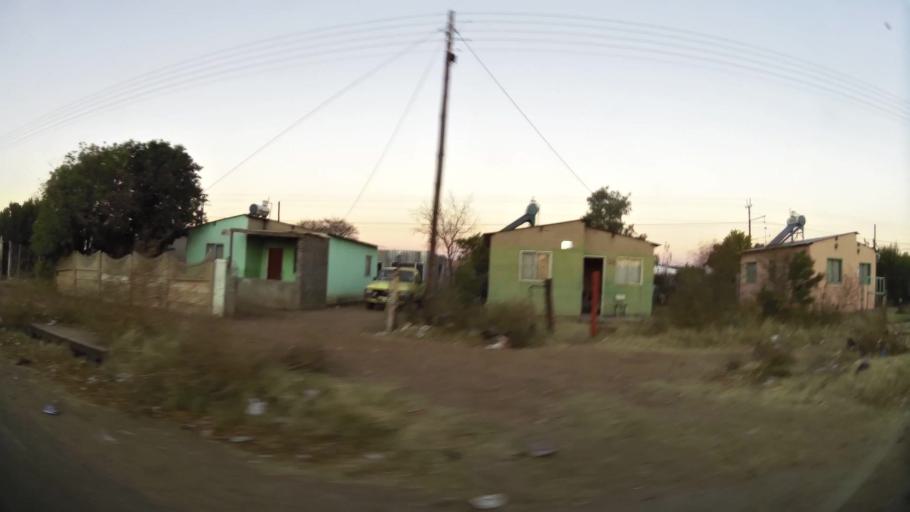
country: ZA
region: Northern Cape
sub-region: Frances Baard District Municipality
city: Kimberley
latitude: -28.7145
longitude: 24.7685
